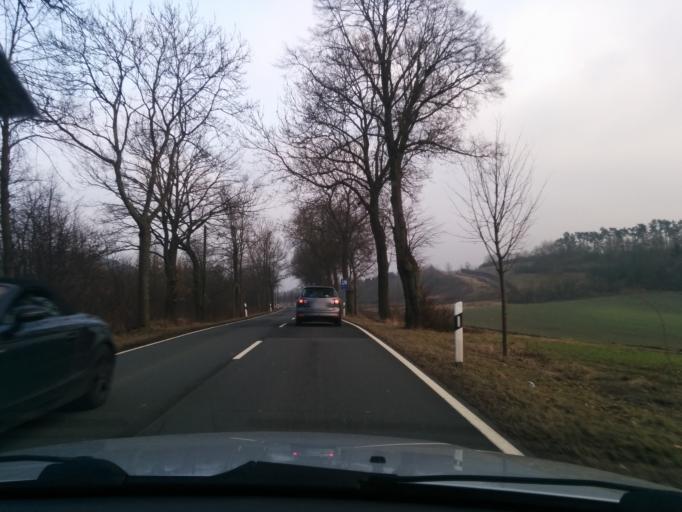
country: DE
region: Thuringia
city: Ifta
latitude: 51.0777
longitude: 10.1487
